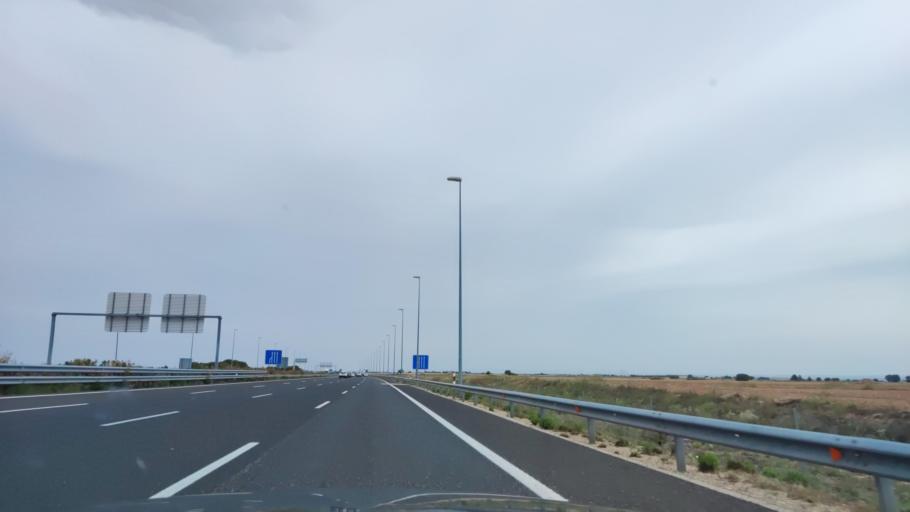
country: ES
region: Castille-La Mancha
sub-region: Provincia de Albacete
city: La Roda
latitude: 39.2470
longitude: -2.2014
